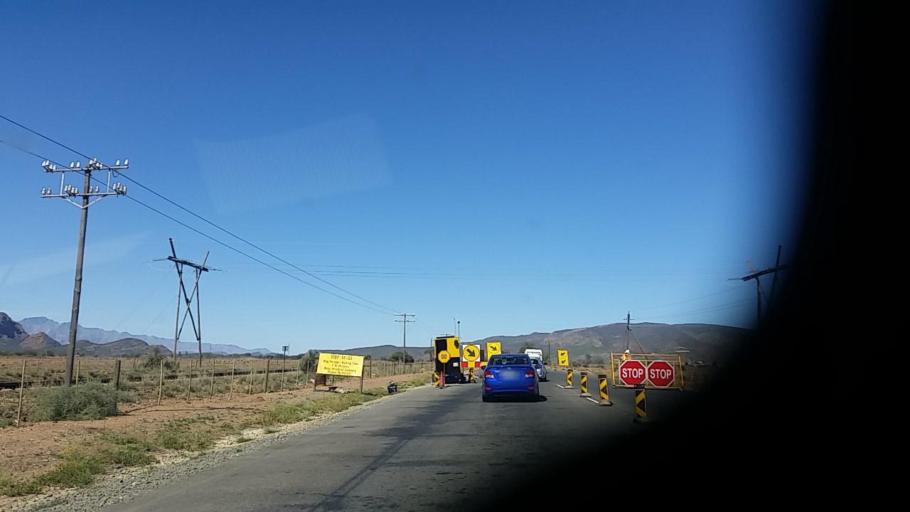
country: ZA
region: Western Cape
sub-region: Eden District Municipality
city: Oudtshoorn
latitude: -33.5612
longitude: 22.3954
